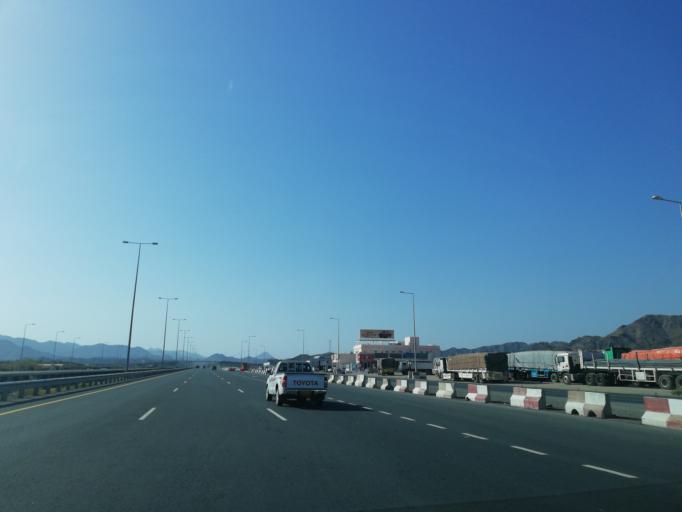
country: OM
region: Muhafazat ad Dakhiliyah
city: Sufalat Sama'il
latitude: 23.0251
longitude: 58.2097
